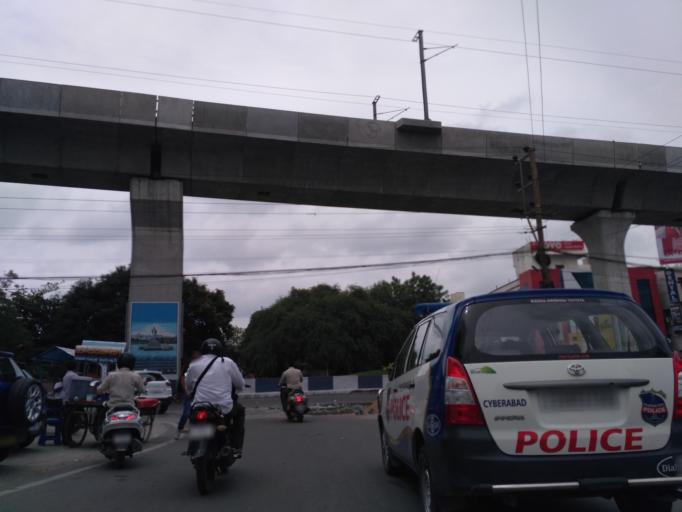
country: IN
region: Telangana
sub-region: Rangareddi
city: Kukatpalli
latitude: 17.4410
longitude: 78.3899
